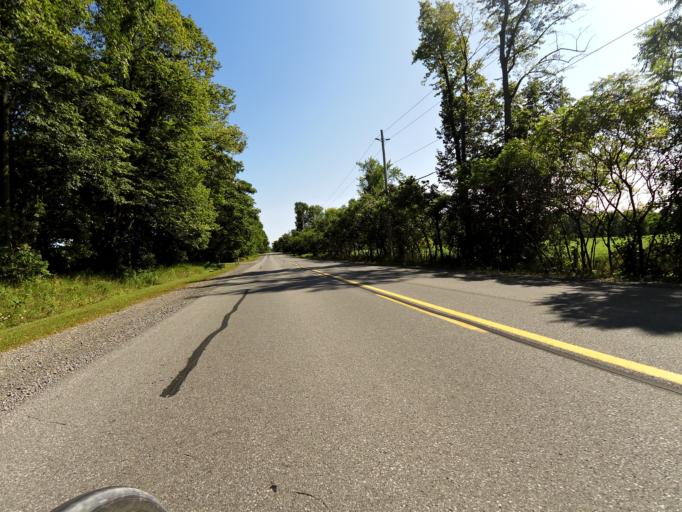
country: CA
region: Ontario
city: Bells Corners
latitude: 45.4110
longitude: -75.9340
